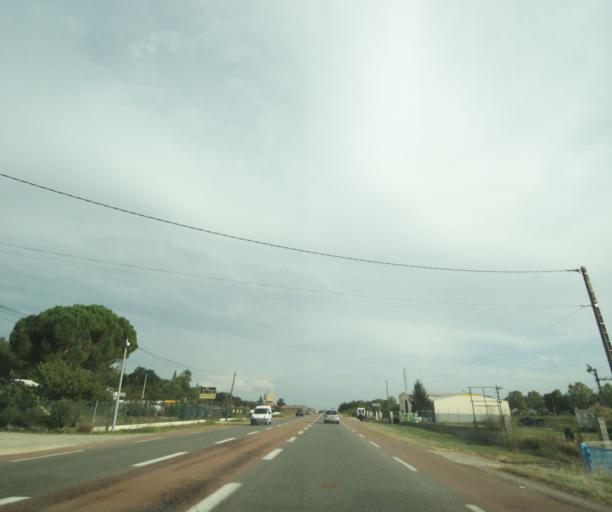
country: FR
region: Midi-Pyrenees
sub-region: Departement du Tarn-et-Garonne
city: Pompignan
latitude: 43.8101
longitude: 1.3188
